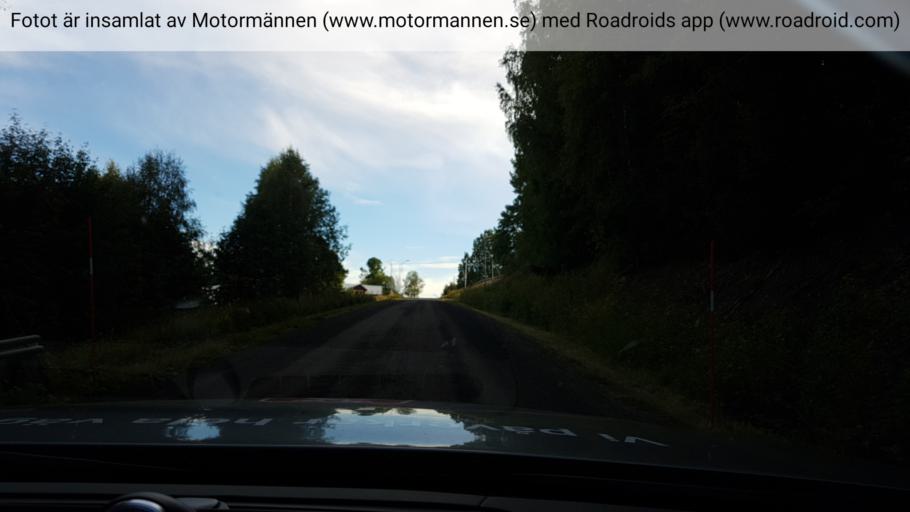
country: SE
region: Jaemtland
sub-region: Stroemsunds Kommun
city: Stroemsund
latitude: 64.0860
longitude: 15.8244
